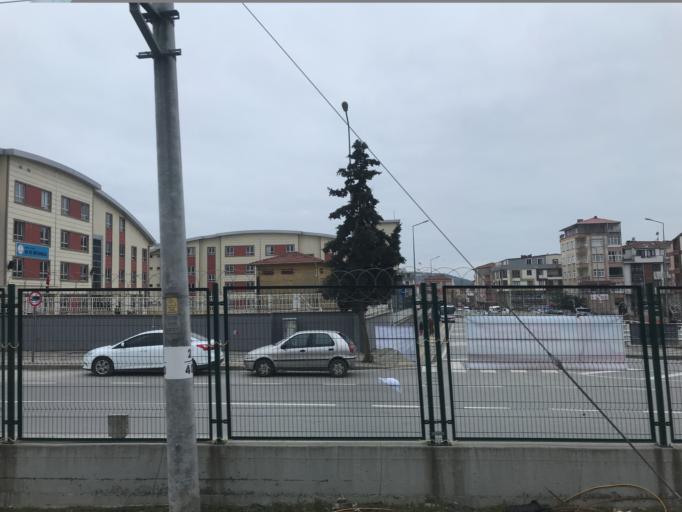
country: TR
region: Kocaeli
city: Darica
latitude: 40.7871
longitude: 29.4002
